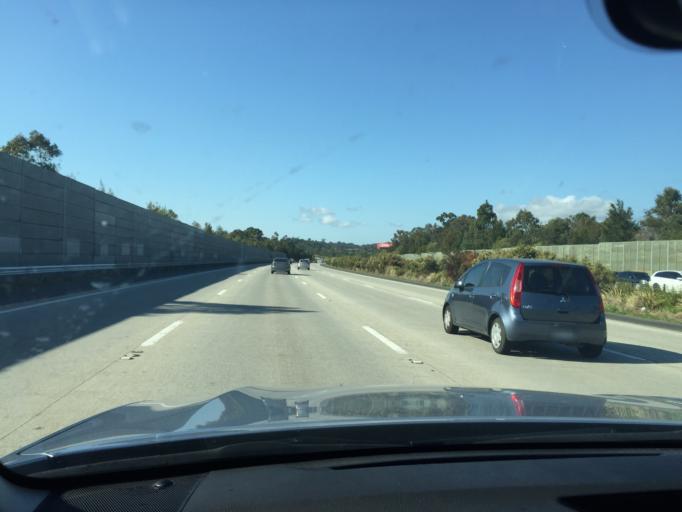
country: AU
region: Queensland
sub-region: Gold Coast
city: Ormeau Hills
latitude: -27.7912
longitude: 153.2594
